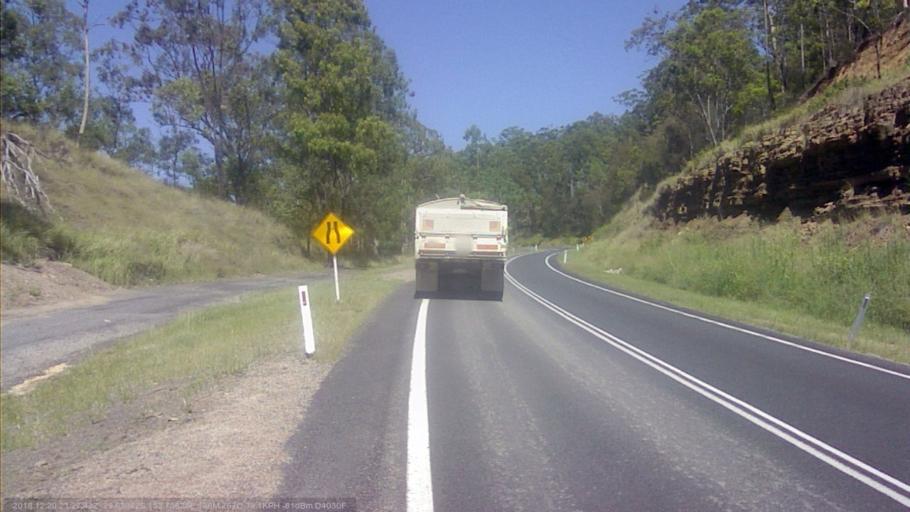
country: AU
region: New South Wales
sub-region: Clarence Valley
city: South Grafton
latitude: -29.6304
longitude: 152.7380
